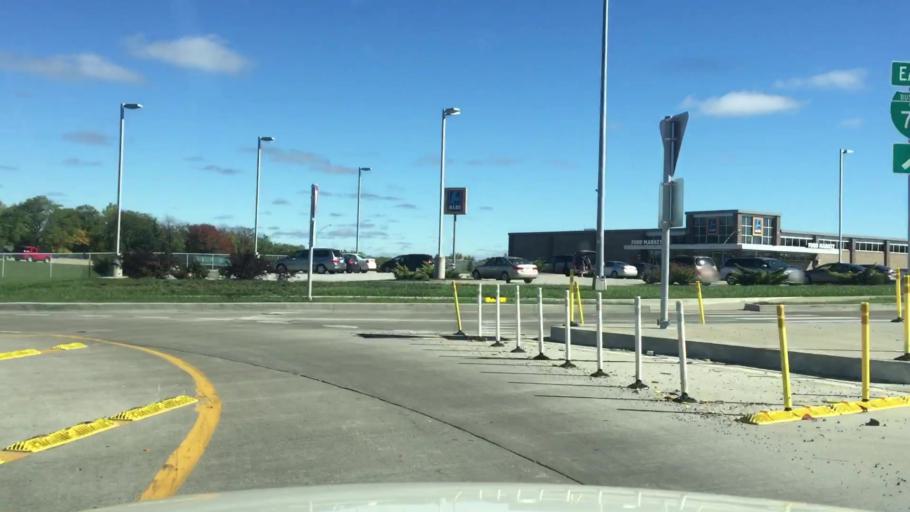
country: US
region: Missouri
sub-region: Boone County
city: Columbia
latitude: 38.9663
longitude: -92.3501
